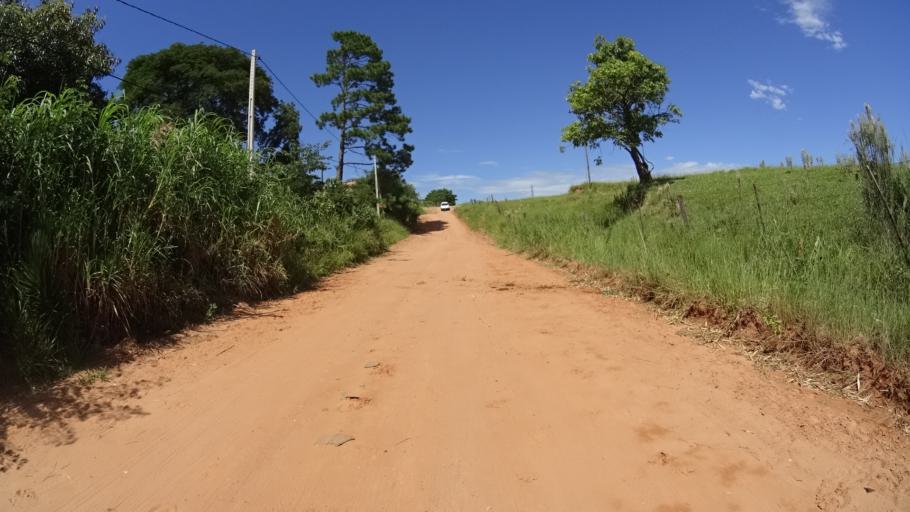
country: BR
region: Sao Paulo
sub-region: Marilia
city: Marilia
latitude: -22.1847
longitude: -49.9799
